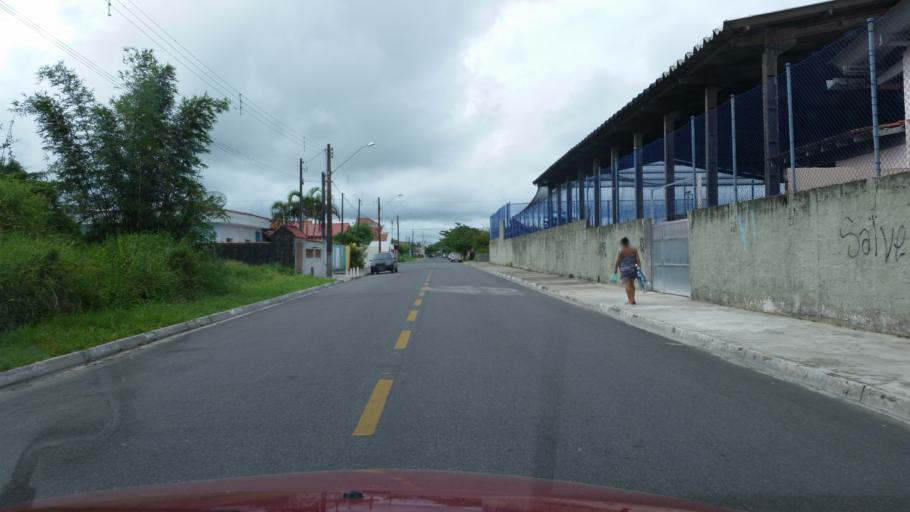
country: BR
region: Sao Paulo
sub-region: Iguape
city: Iguape
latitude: -24.7454
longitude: -47.5544
